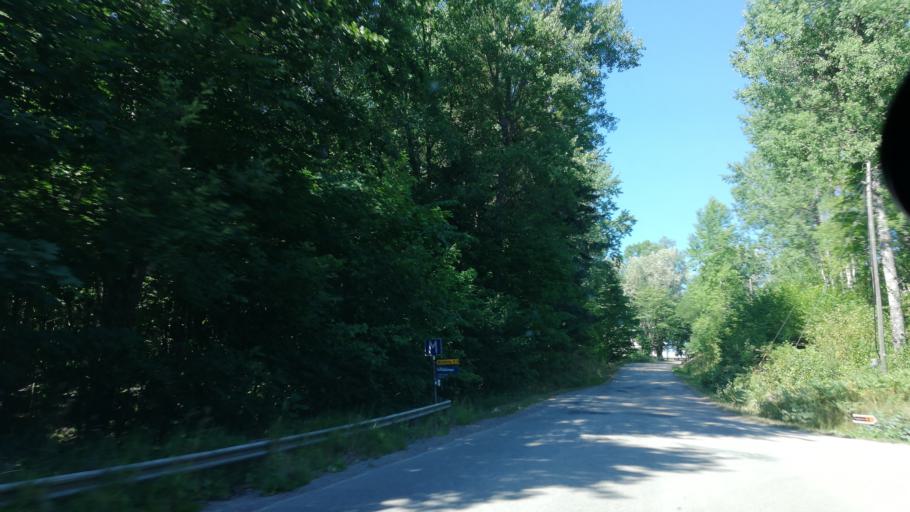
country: SE
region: OEstergoetland
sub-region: Finspangs Kommun
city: Finspang
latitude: 58.7318
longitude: 15.7293
